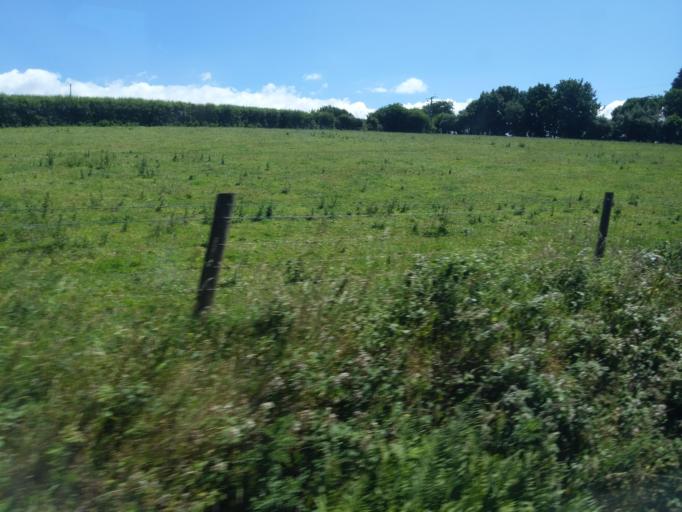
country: GB
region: England
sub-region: Cornwall
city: Saint Stephen
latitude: 50.3296
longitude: -4.8573
